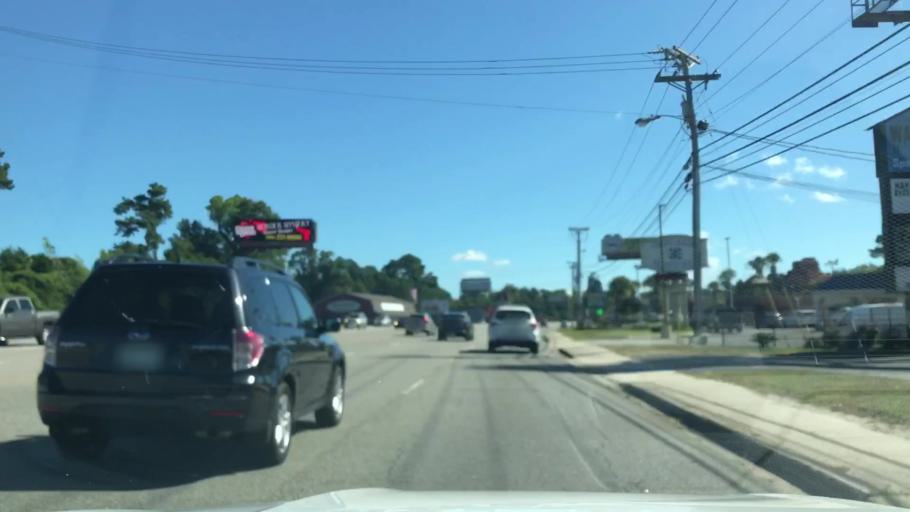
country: US
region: South Carolina
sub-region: Horry County
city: North Myrtle Beach
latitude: 33.7820
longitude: -78.7879
